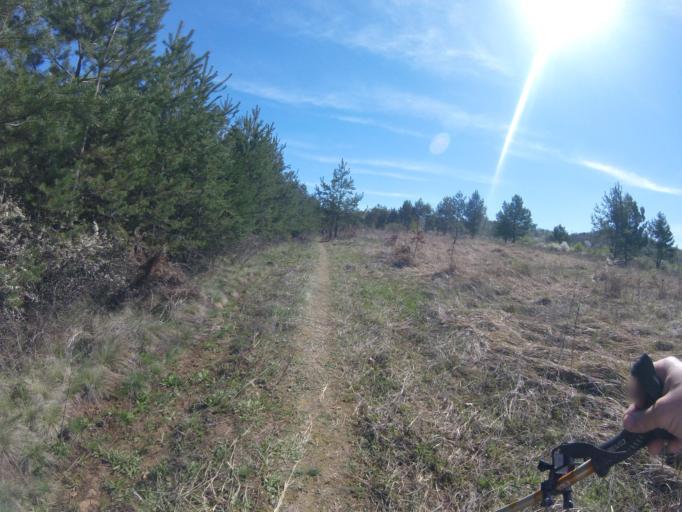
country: HU
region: Borsod-Abauj-Zemplen
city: Szendro
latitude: 48.4064
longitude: 20.7518
